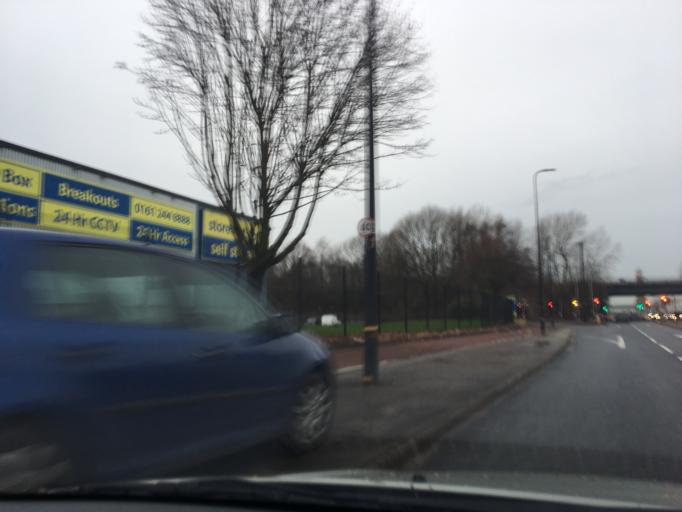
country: GB
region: England
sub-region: Trafford
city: Stretford
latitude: 53.4615
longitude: -2.3327
